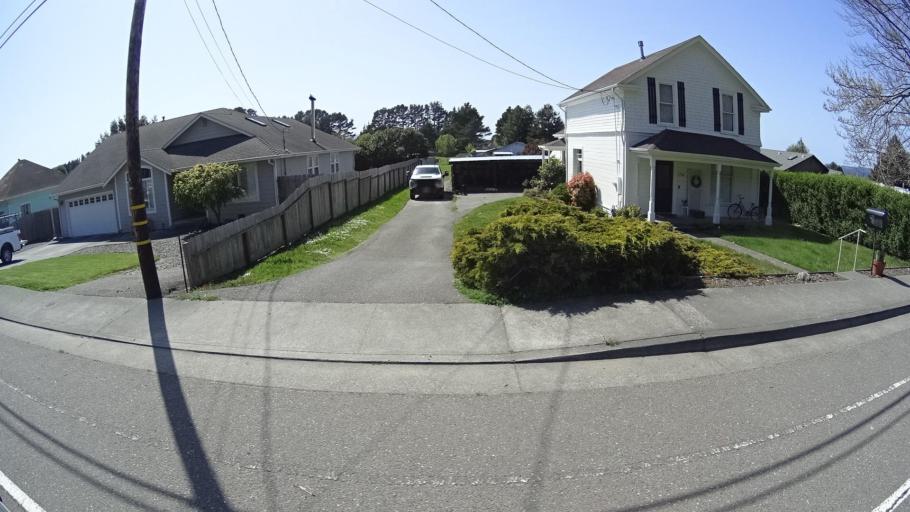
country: US
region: California
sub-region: Humboldt County
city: Hydesville
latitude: 40.5667
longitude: -124.1267
